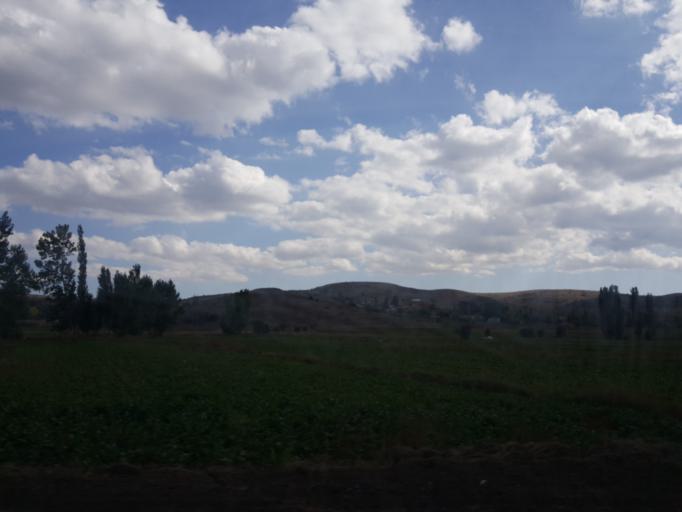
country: TR
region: Tokat
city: Yesilyurt
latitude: 40.0264
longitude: 36.2974
